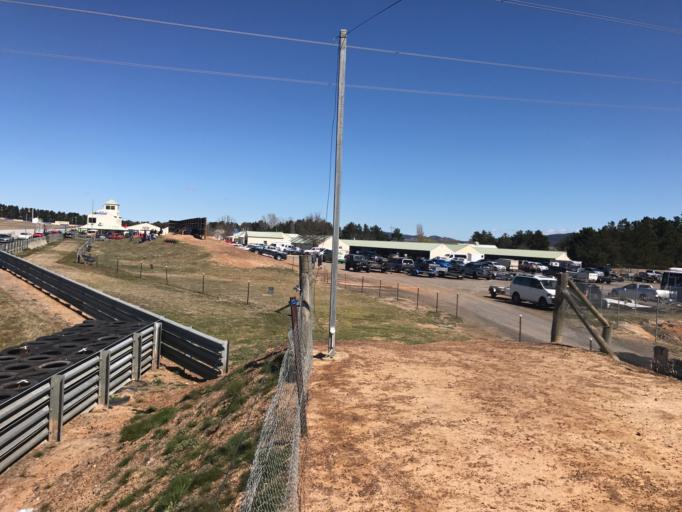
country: AU
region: New South Wales
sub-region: Goulburn Mulwaree
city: Goulburn
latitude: -34.8386
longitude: 149.6857
